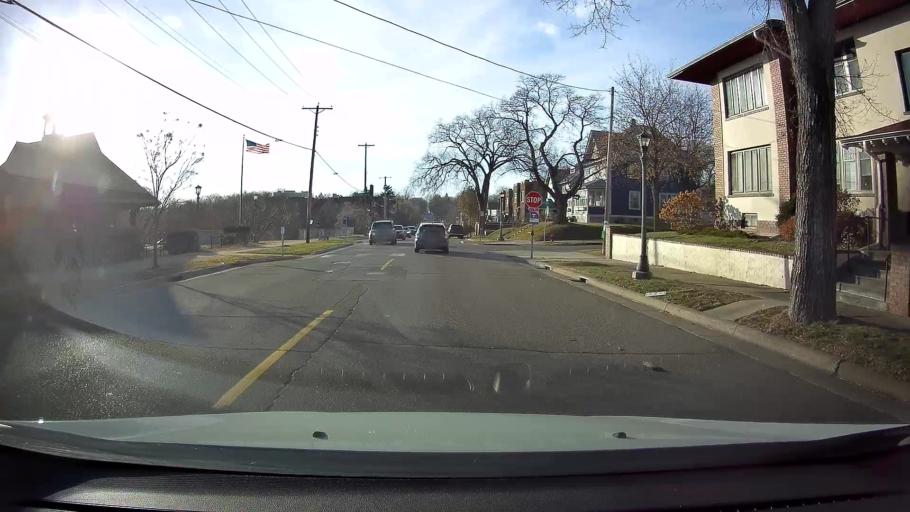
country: US
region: Minnesota
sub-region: Dakota County
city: West Saint Paul
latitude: 44.9341
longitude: -93.1359
